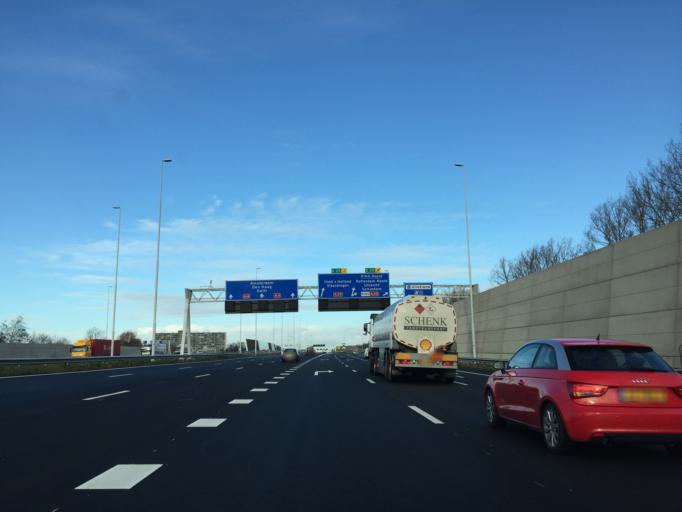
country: NL
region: South Holland
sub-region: Gemeente Schiedam
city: Schiedam
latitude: 51.9200
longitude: 4.3667
